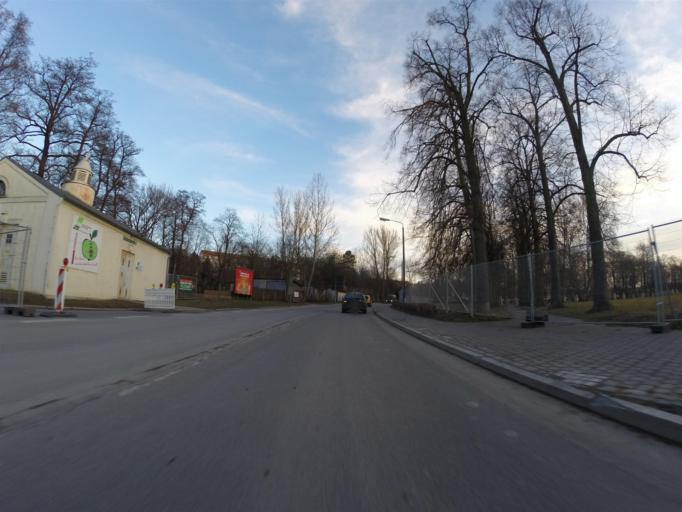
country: DE
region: Thuringia
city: Apolda
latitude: 51.0212
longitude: 11.5097
